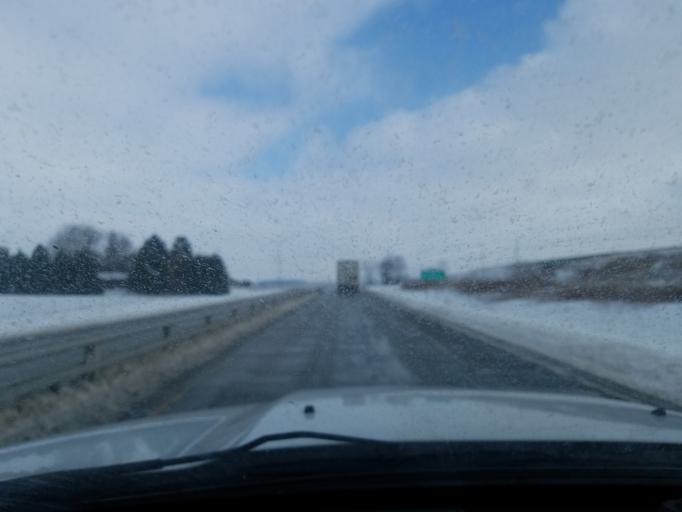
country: US
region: Indiana
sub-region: Marshall County
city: Bremen
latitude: 41.4614
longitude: -86.1576
